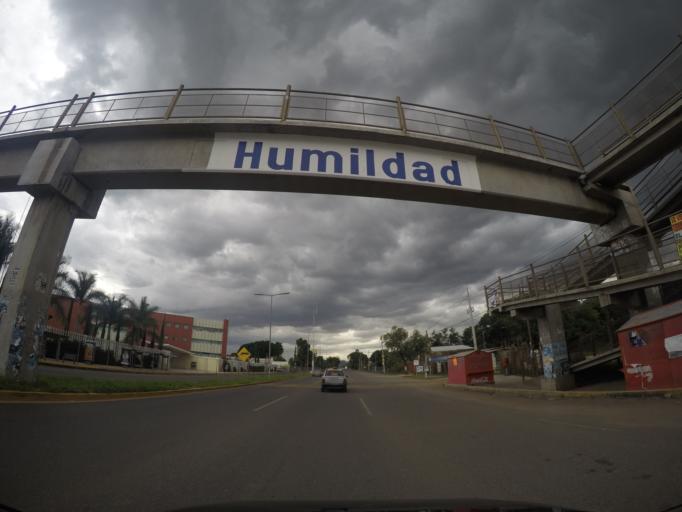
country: MX
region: Oaxaca
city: Tlalixtac de Cabrera
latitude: 17.0555
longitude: -96.6536
